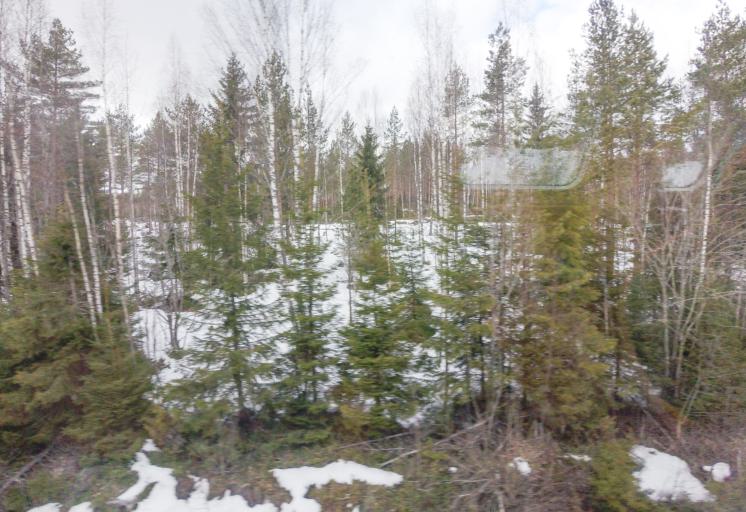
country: FI
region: South Karelia
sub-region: Imatra
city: Rautjaervi
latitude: 61.3201
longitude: 29.1403
